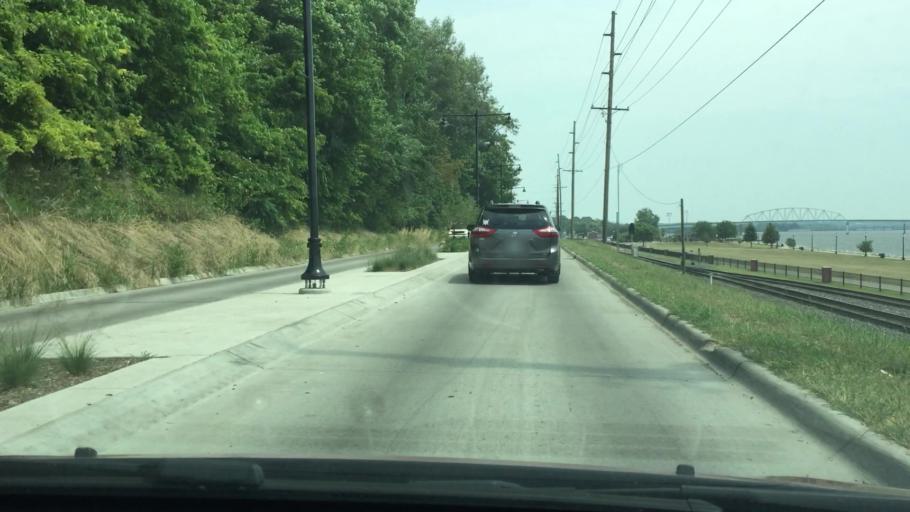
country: US
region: Iowa
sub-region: Muscatine County
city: Muscatine
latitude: 41.4171
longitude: -91.0509
